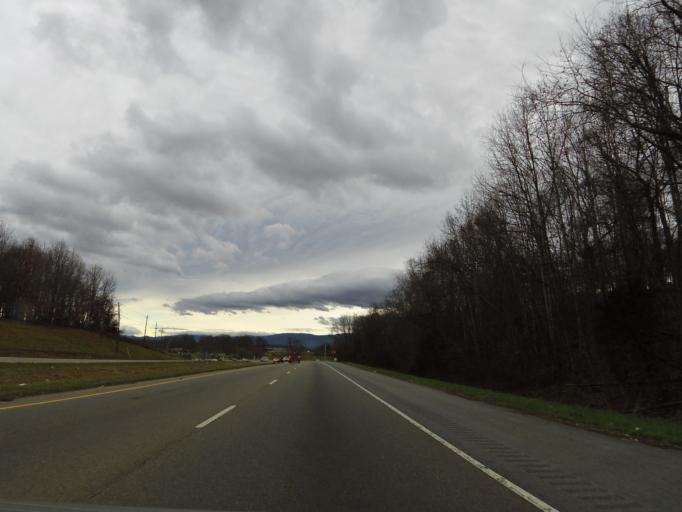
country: US
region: Tennessee
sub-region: Greene County
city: Tusculum
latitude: 36.1826
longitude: -82.7523
